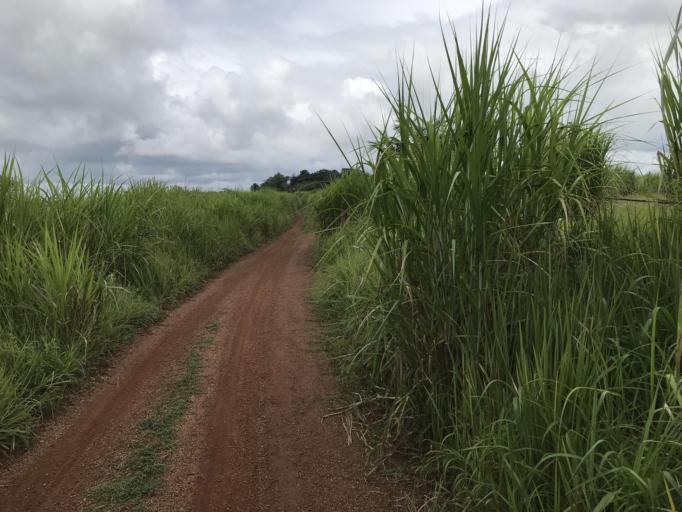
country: SL
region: Eastern Province
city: Buedu
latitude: 8.4714
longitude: -10.3191
